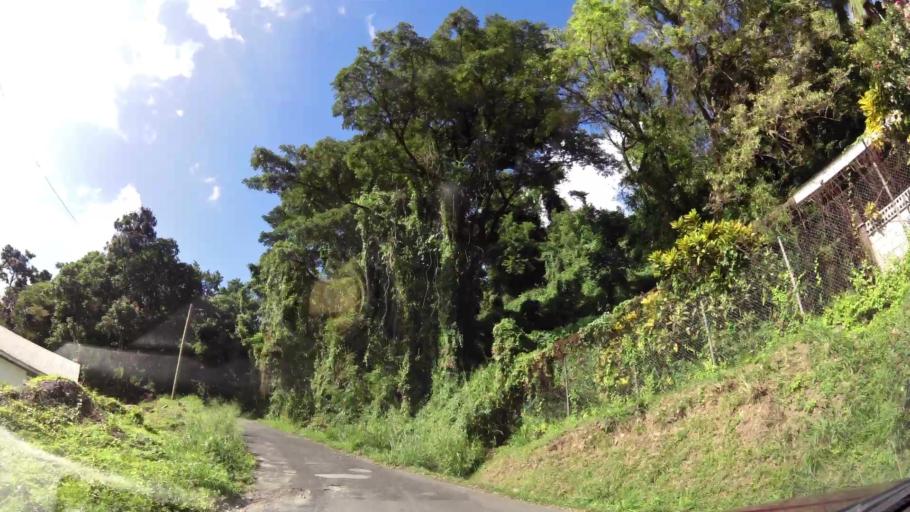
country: DM
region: Saint Luke
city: Pointe Michel
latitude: 15.2793
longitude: -61.3715
